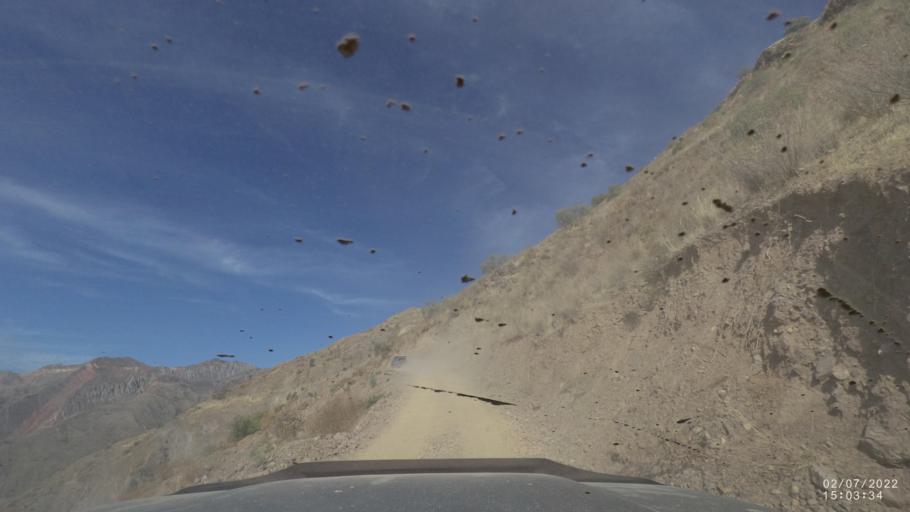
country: BO
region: Cochabamba
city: Irpa Irpa
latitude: -17.8582
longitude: -66.4388
